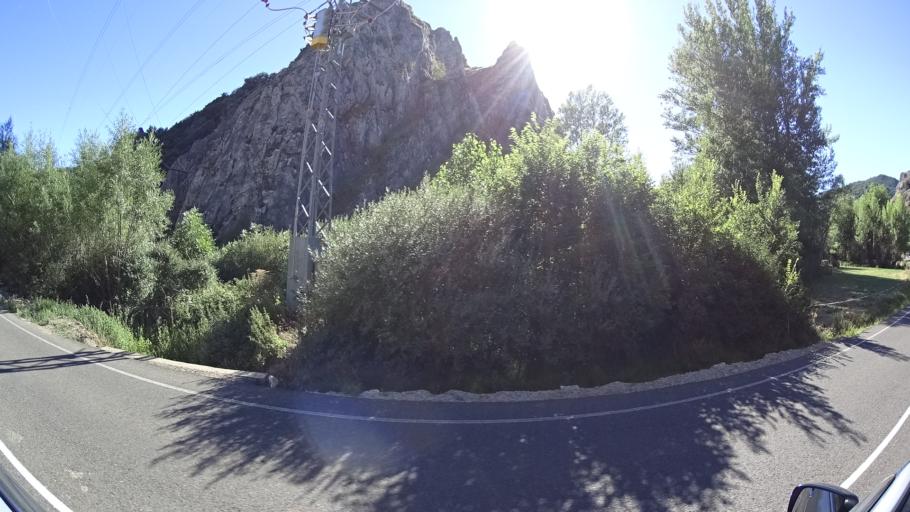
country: ES
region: Castille and Leon
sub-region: Provincia de Leon
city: La Pola de Gordon
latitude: 42.8682
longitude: -5.6816
